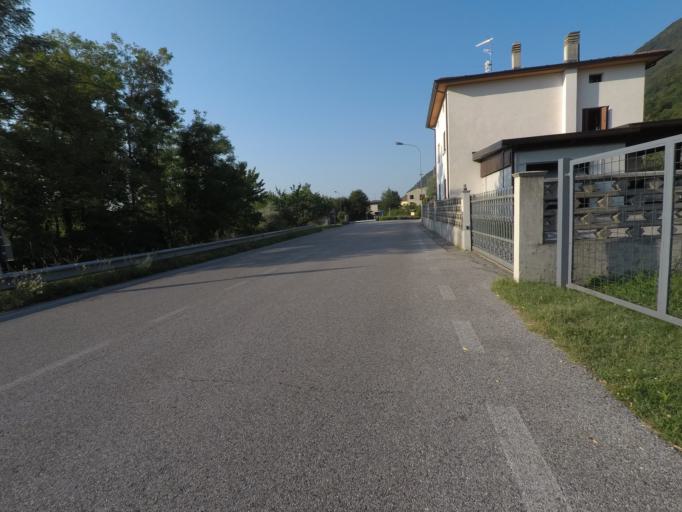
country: IT
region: Friuli Venezia Giulia
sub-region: Provincia di Udine
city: Trasaghis
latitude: 46.2612
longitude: 13.0406
